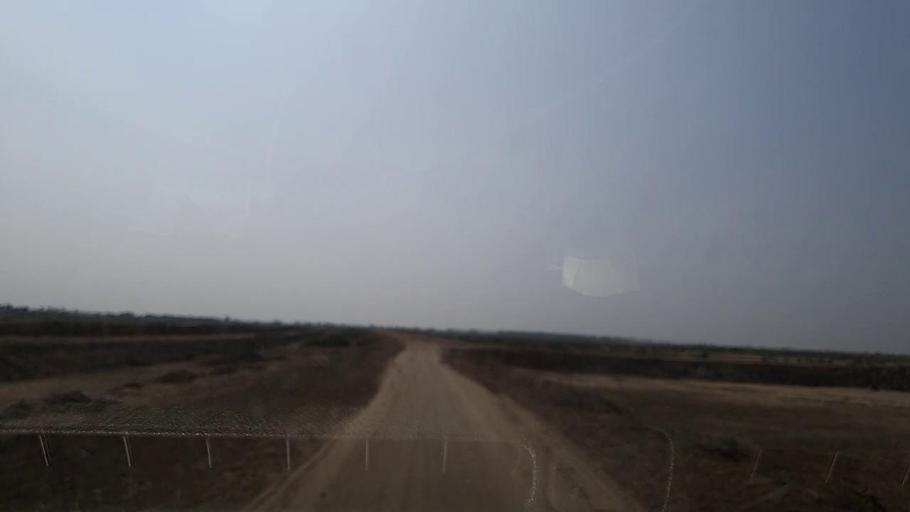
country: PK
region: Sindh
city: Mirpur Sakro
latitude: 24.5373
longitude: 67.7838
